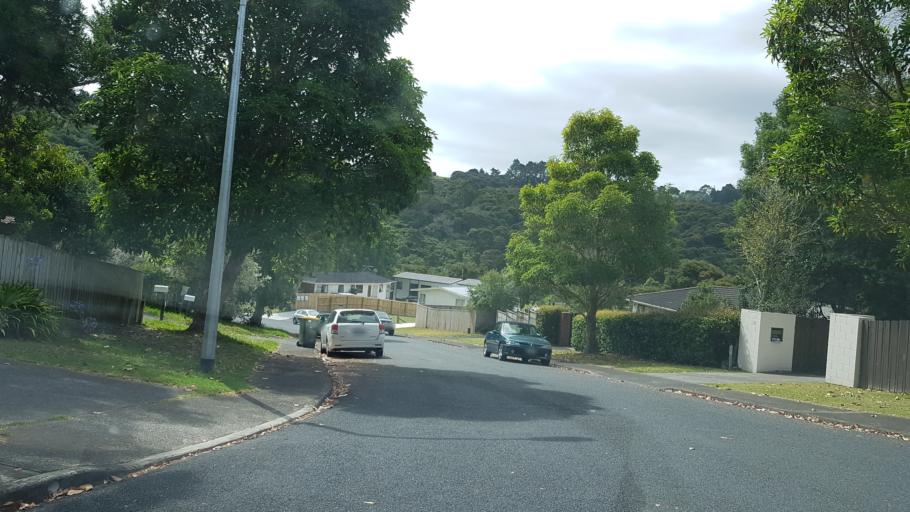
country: NZ
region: Auckland
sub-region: Auckland
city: North Shore
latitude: -36.7715
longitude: 174.7076
